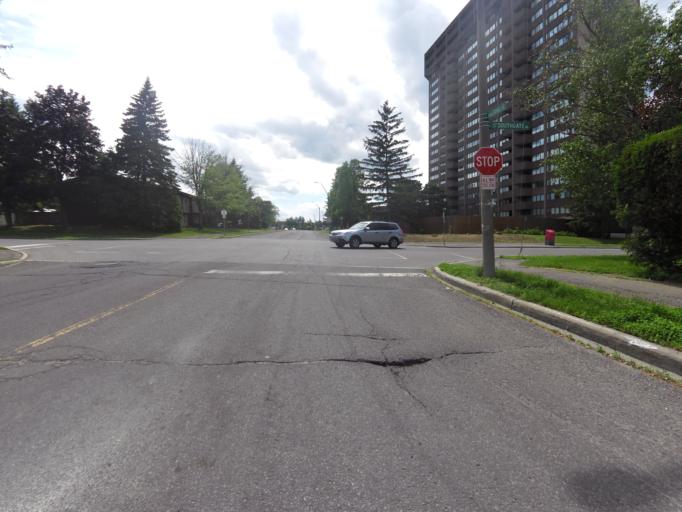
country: CA
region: Ontario
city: Ottawa
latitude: 45.3567
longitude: -75.6493
